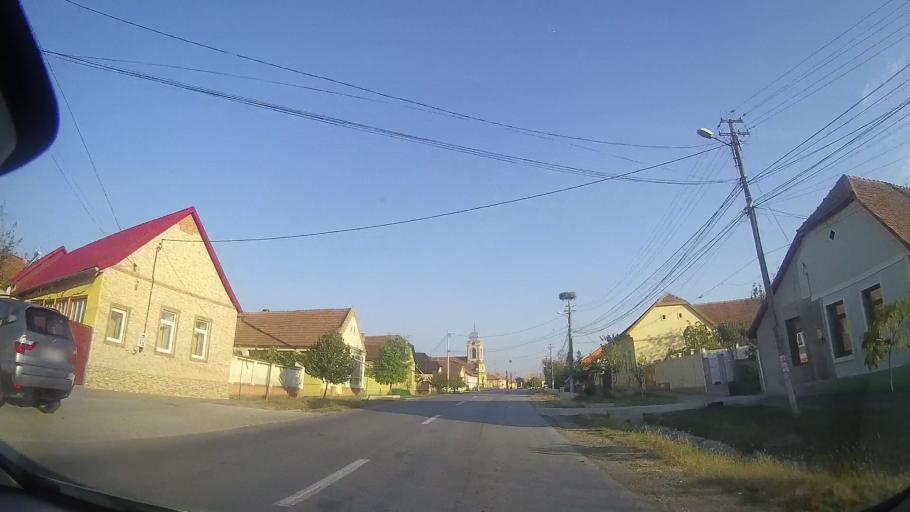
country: RO
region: Timis
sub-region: Comuna Pischia
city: Pischia
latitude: 45.9007
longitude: 21.3404
